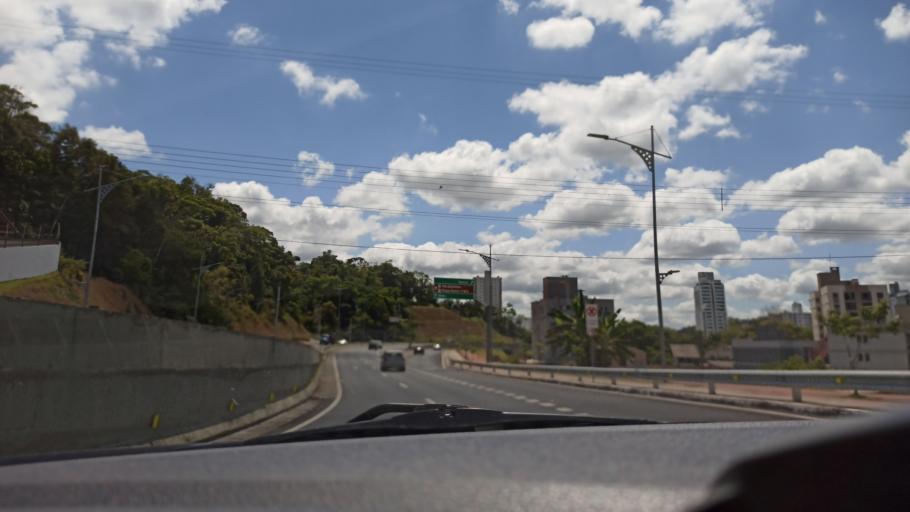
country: BR
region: Santa Catarina
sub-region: Blumenau
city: Blumenau
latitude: -26.9162
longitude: -49.0980
